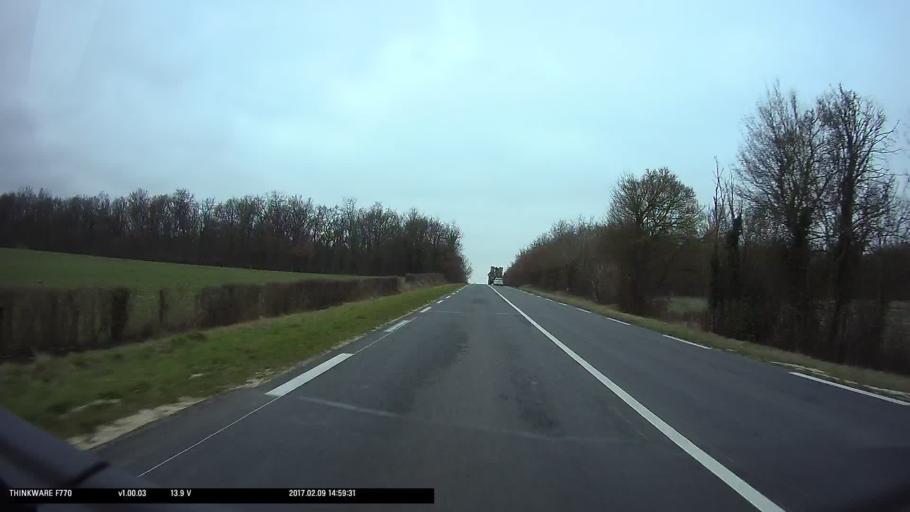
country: FR
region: Centre
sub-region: Departement du Cher
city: Levet
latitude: 46.8247
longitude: 2.4245
